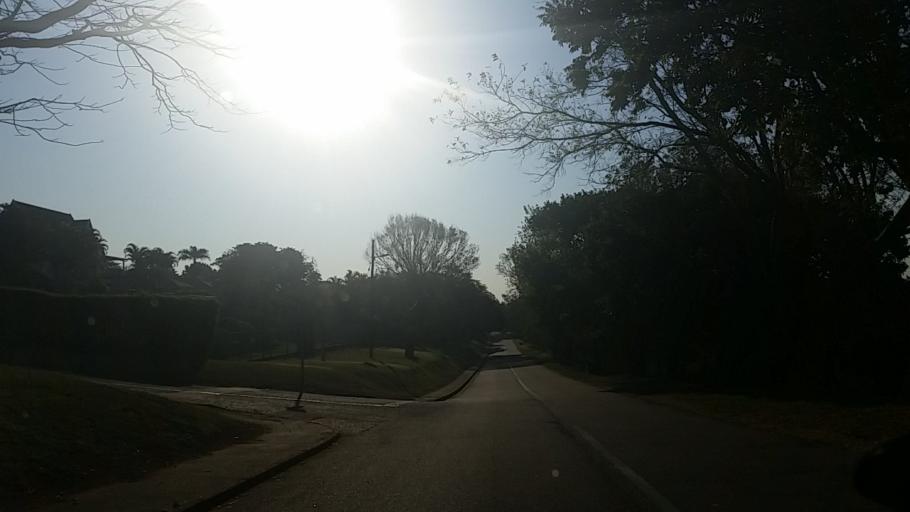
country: ZA
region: KwaZulu-Natal
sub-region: eThekwini Metropolitan Municipality
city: Berea
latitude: -29.8442
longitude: 30.9249
